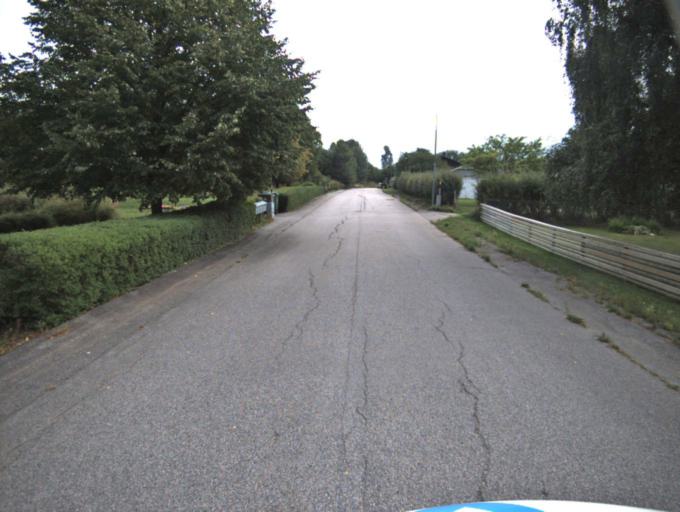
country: SE
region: Vaestra Goetaland
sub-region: Ulricehamns Kommun
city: Ulricehamn
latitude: 57.8410
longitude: 13.2878
